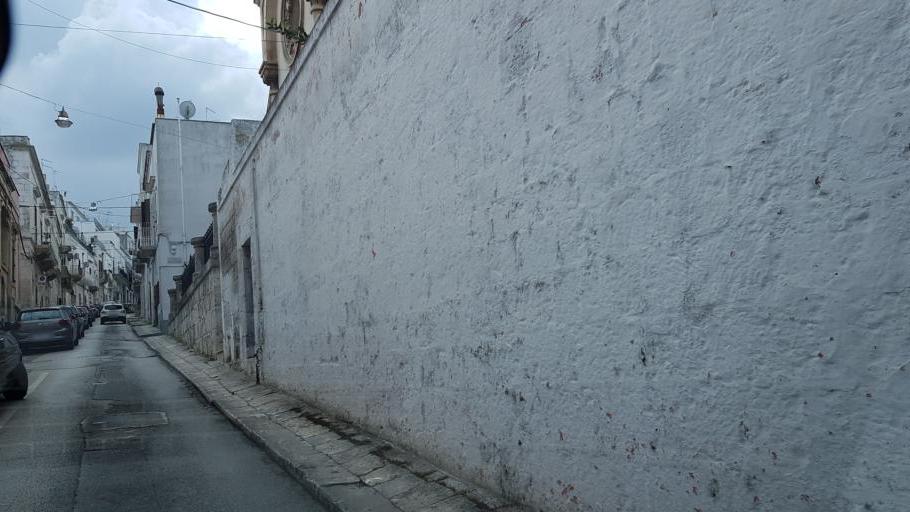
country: IT
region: Apulia
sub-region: Provincia di Brindisi
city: Ostuni
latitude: 40.7309
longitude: 17.5746
